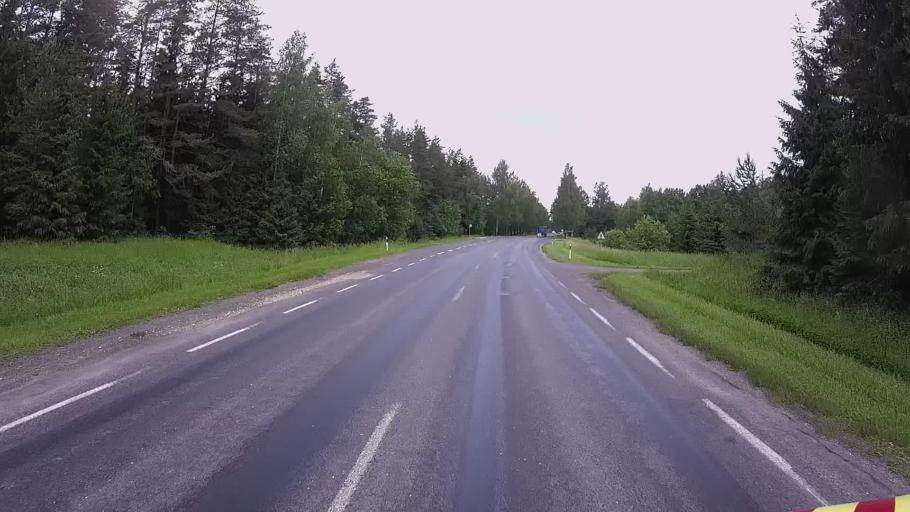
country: EE
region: Viljandimaa
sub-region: Viljandi linn
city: Viljandi
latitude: 58.2984
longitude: 25.5753
